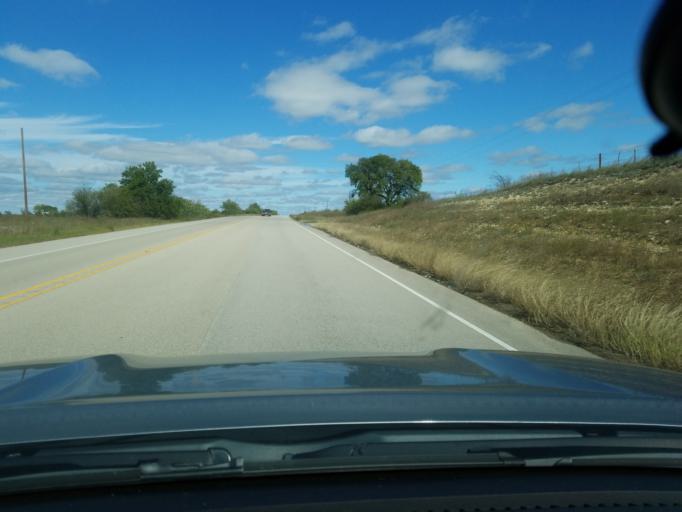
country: US
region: Texas
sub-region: Hamilton County
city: Hamilton
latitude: 31.6574
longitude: -98.1434
